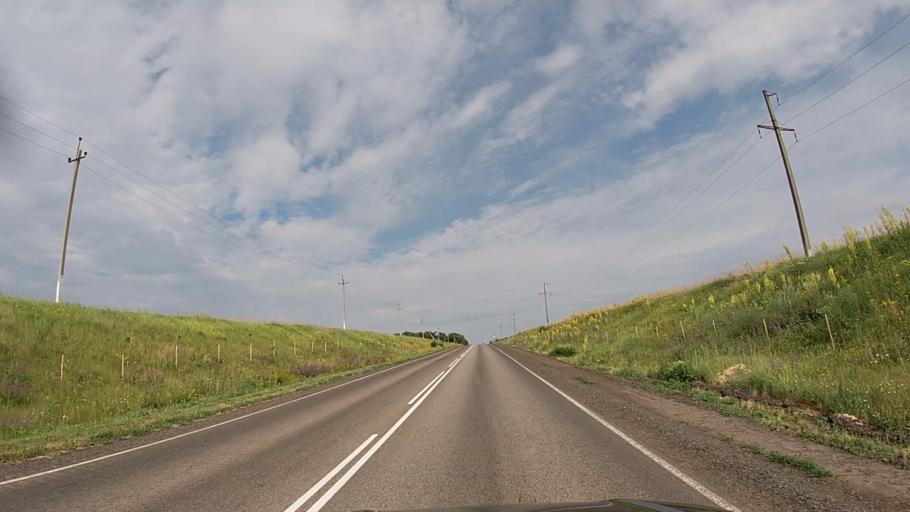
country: RU
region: Belgorod
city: Krasnaya Yaruga
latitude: 50.8003
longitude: 35.5671
